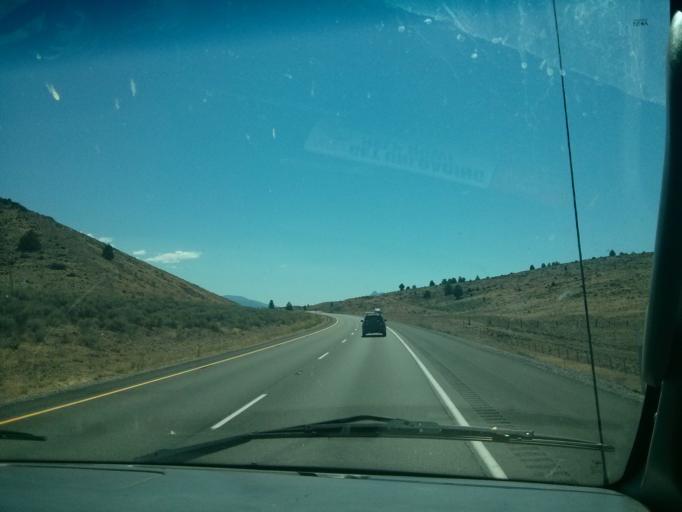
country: US
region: California
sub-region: Siskiyou County
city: Weed
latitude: 41.5027
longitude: -122.4699
